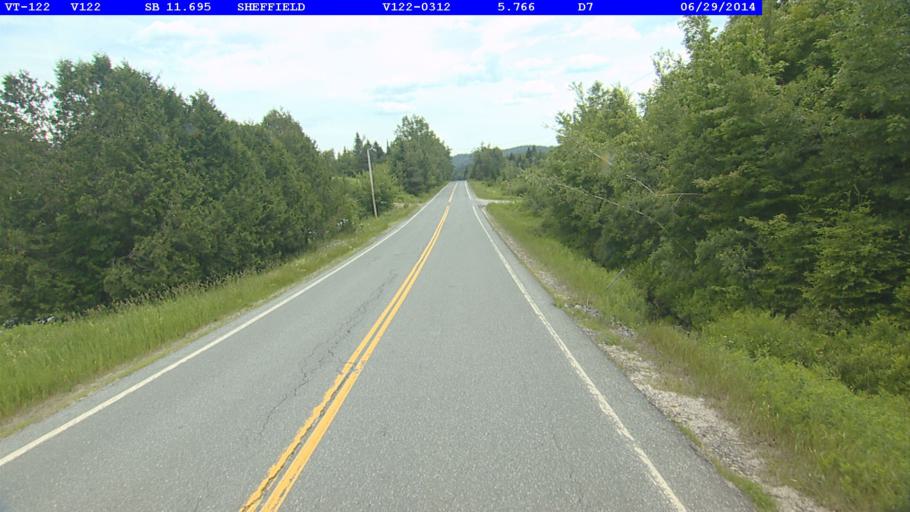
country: US
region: Vermont
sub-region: Caledonia County
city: Lyndonville
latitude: 44.6515
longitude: -72.1616
